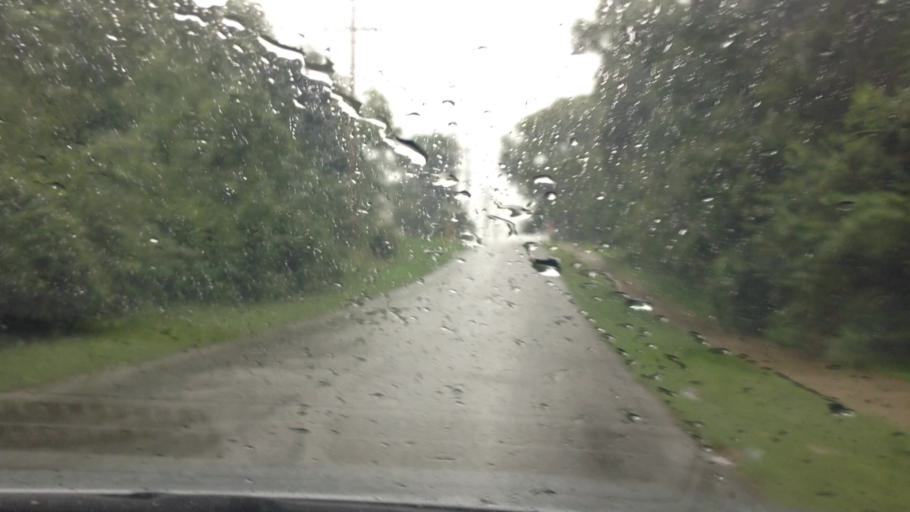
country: US
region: Kansas
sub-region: Leavenworth County
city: Leavenworth
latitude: 39.2950
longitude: -94.9127
